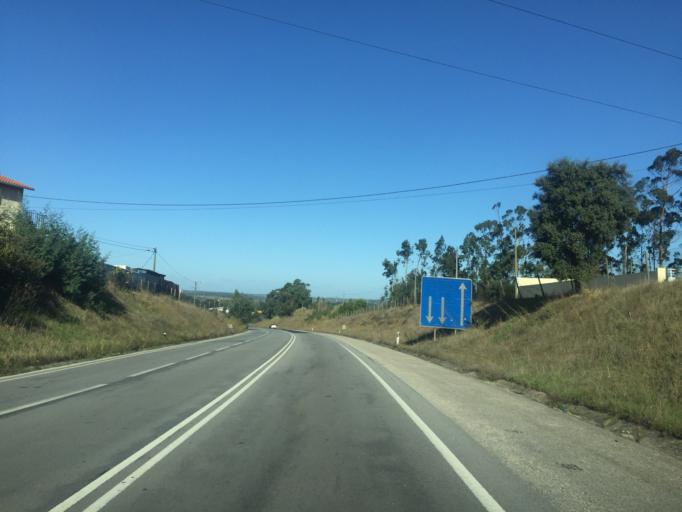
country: PT
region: Leiria
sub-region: Leiria
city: Leiria
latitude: 39.7732
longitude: -8.8169
